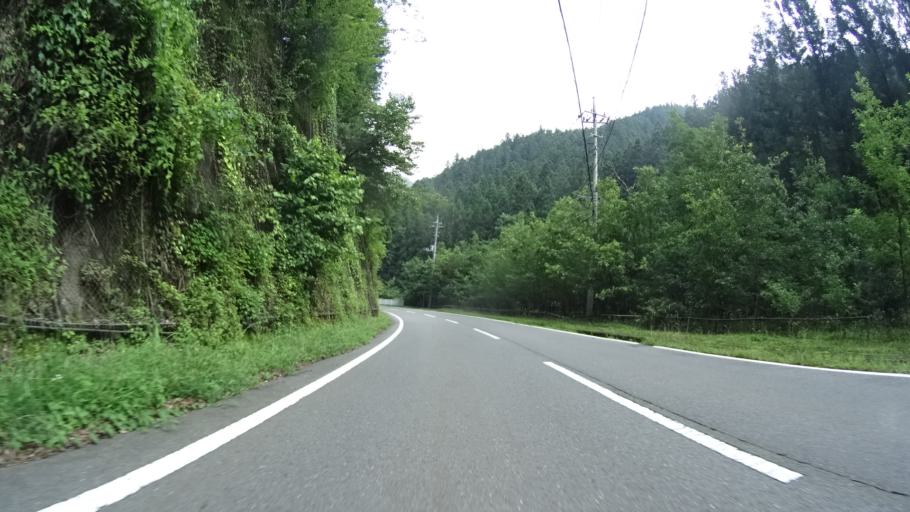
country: JP
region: Gunma
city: Tomioka
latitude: 36.0795
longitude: 138.8251
